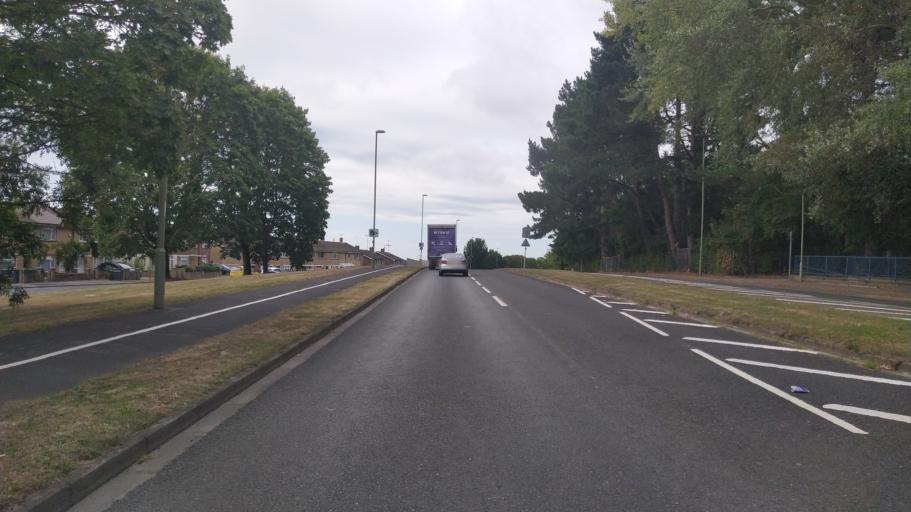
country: GB
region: England
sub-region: Hampshire
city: Havant
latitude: 50.8733
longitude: -0.9737
